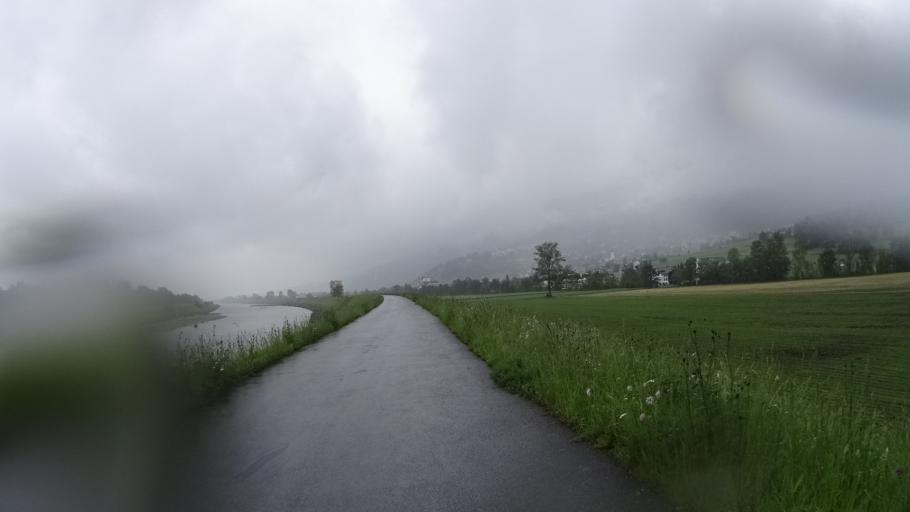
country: LI
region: Triesen
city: Triesen
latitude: 47.0957
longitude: 9.5200
